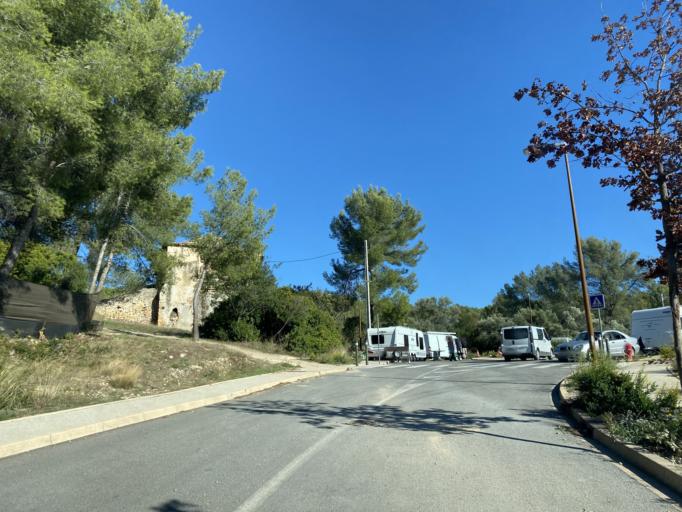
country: FR
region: Provence-Alpes-Cote d'Azur
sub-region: Departement des Bouches-du-Rhone
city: Ceyreste
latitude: 43.2144
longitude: 5.6013
